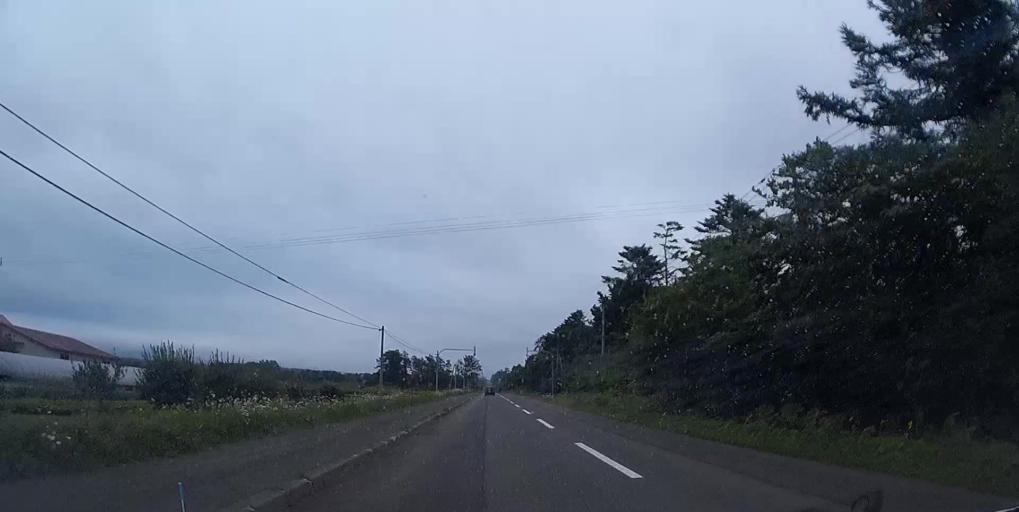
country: JP
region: Hokkaido
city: Iwanai
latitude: 42.4331
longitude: 139.9630
